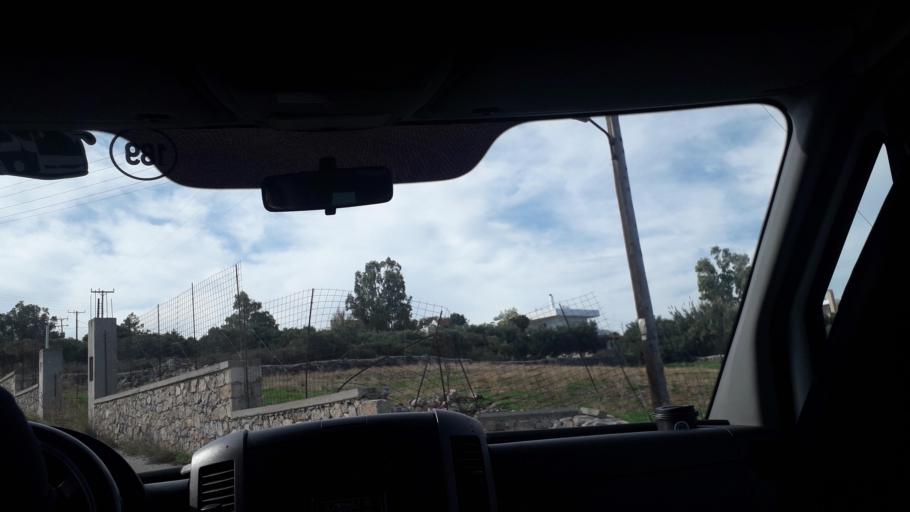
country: GR
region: Crete
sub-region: Nomos Rethymnis
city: Atsipopoulon
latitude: 35.3633
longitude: 24.4344
